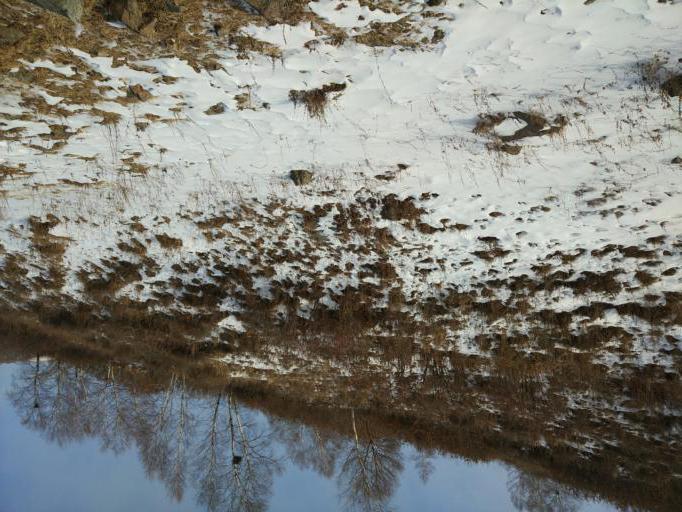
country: CN
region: Hebei
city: Xiwanzi
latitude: 40.8551
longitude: 115.4581
